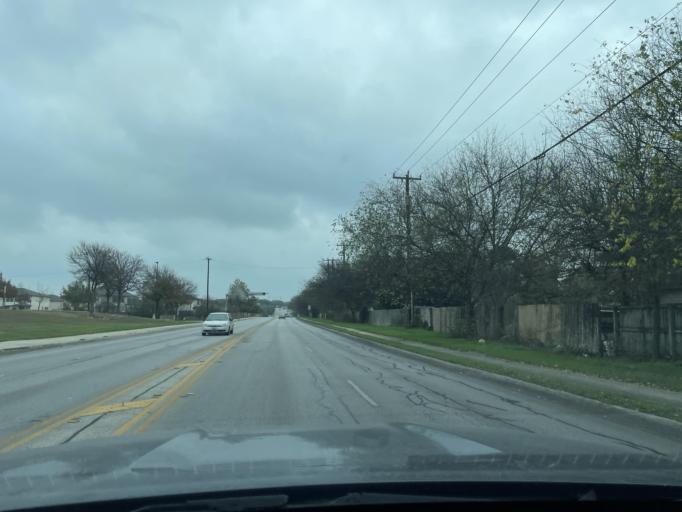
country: US
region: Texas
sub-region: Bexar County
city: Leon Valley
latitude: 29.5572
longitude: -98.6234
